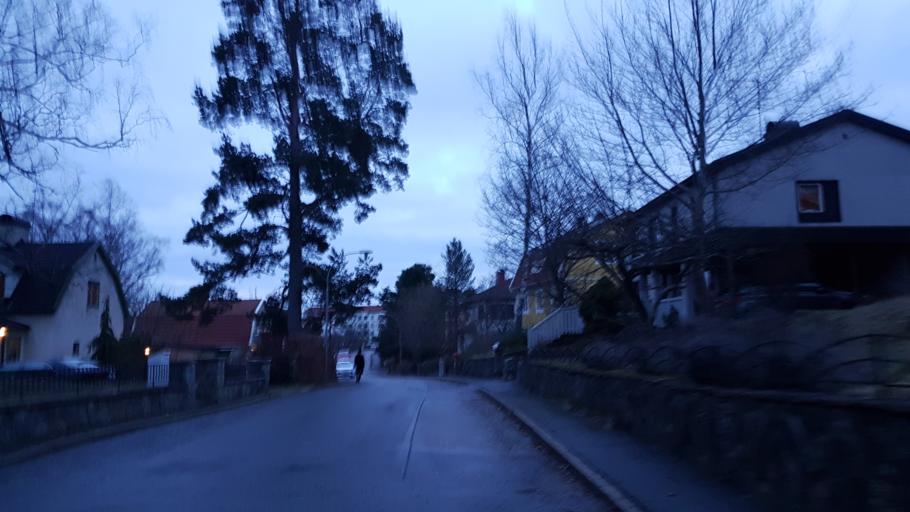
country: SE
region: Stockholm
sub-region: Stockholms Kommun
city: Arsta
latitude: 59.2768
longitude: 18.0512
